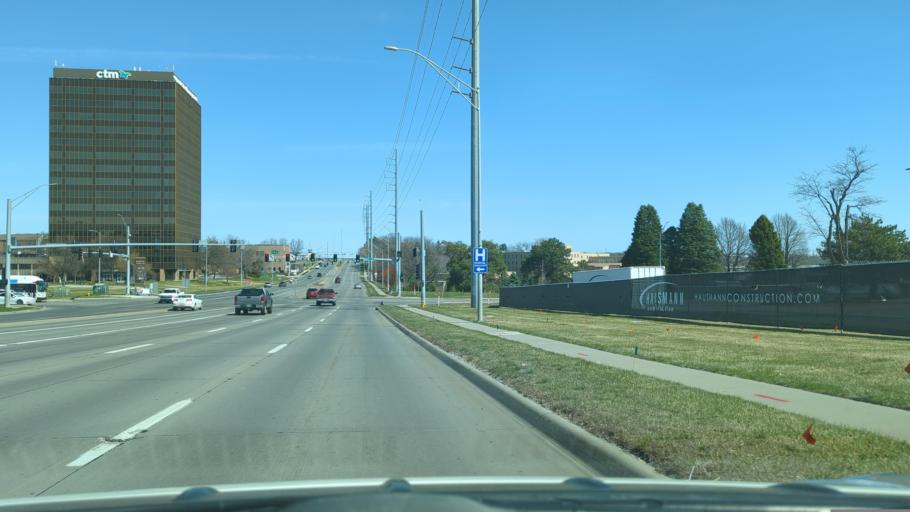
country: US
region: Nebraska
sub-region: Douglas County
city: Ralston
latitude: 41.2369
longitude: -96.0238
